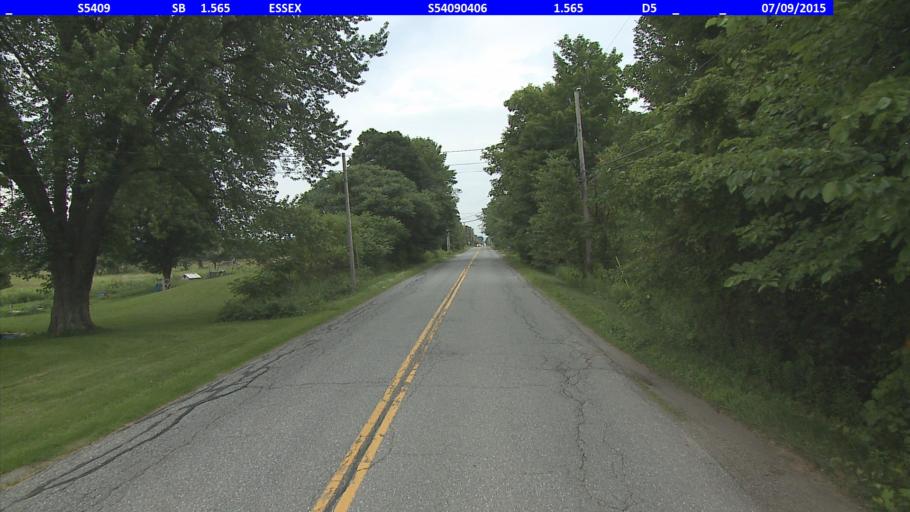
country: US
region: Vermont
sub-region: Chittenden County
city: Essex Junction
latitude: 44.5318
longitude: -73.0763
